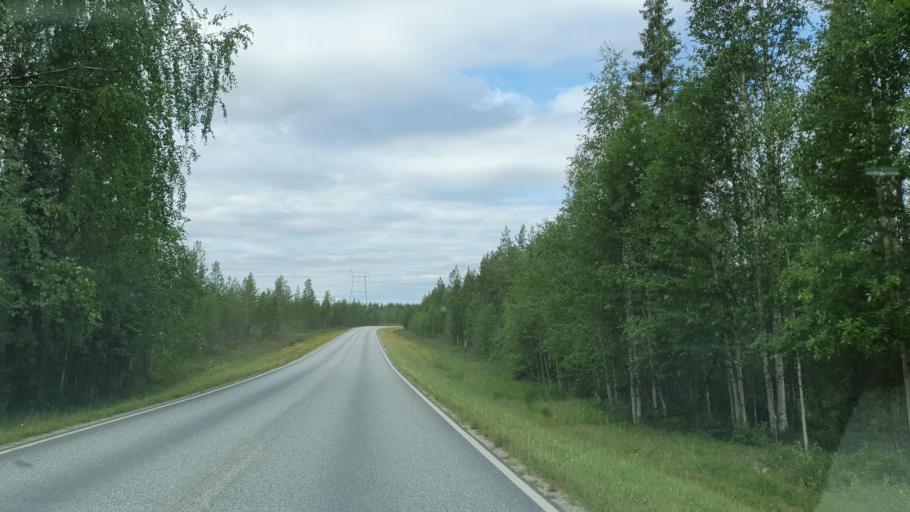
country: FI
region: Lapland
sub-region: Tunturi-Lappi
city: Kittilae
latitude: 67.6087
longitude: 25.2650
